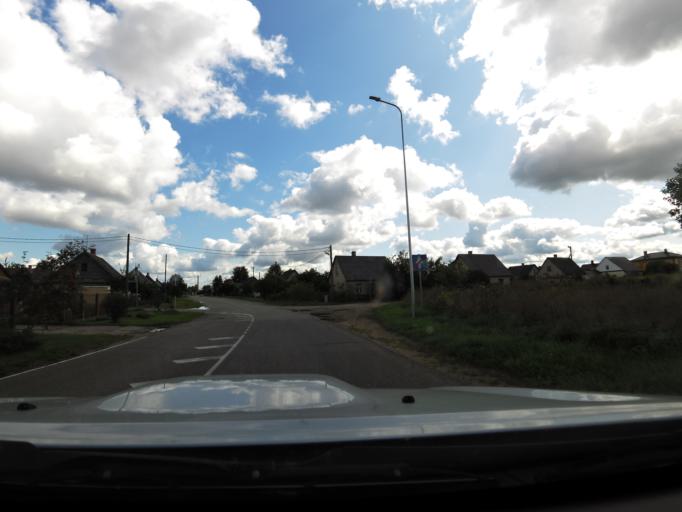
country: LV
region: Daugavpils
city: Daugavpils
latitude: 55.8649
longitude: 26.4935
